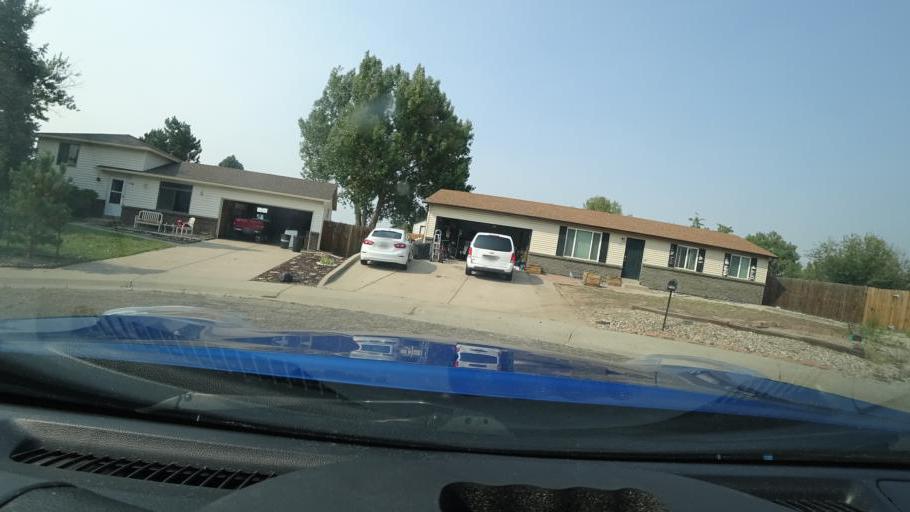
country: US
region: Colorado
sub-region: Adams County
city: Aurora
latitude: 39.6662
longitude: -104.8046
